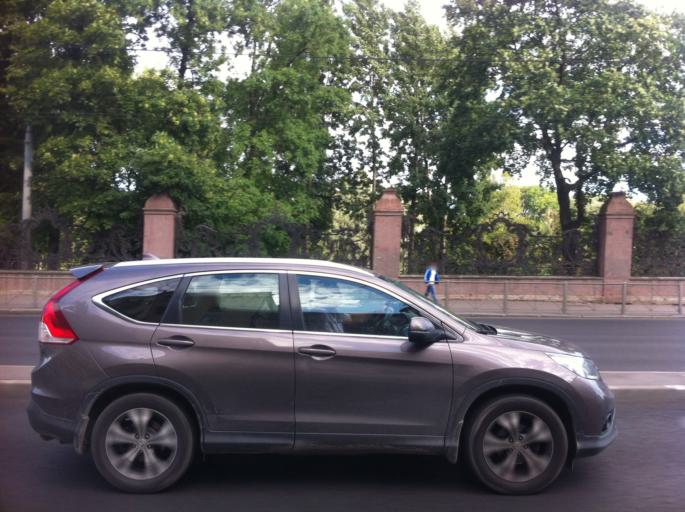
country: RU
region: St.-Petersburg
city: Admiralteisky
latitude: 59.8923
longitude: 30.2735
